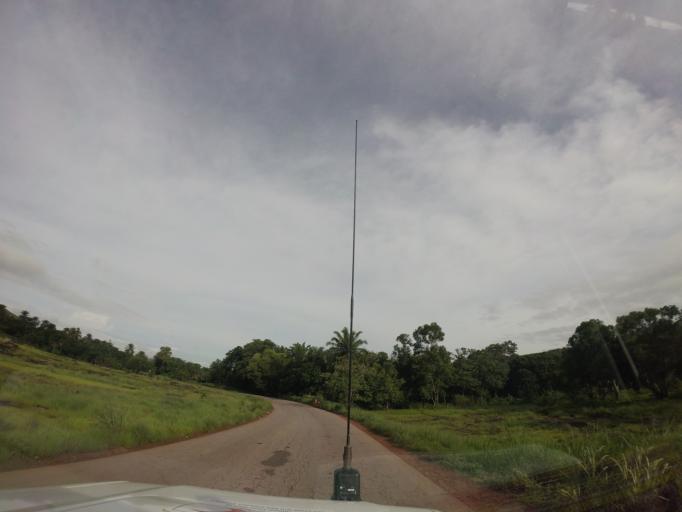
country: GN
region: Kindia
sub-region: Kindia
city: Kindia
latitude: 9.9051
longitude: -13.0118
